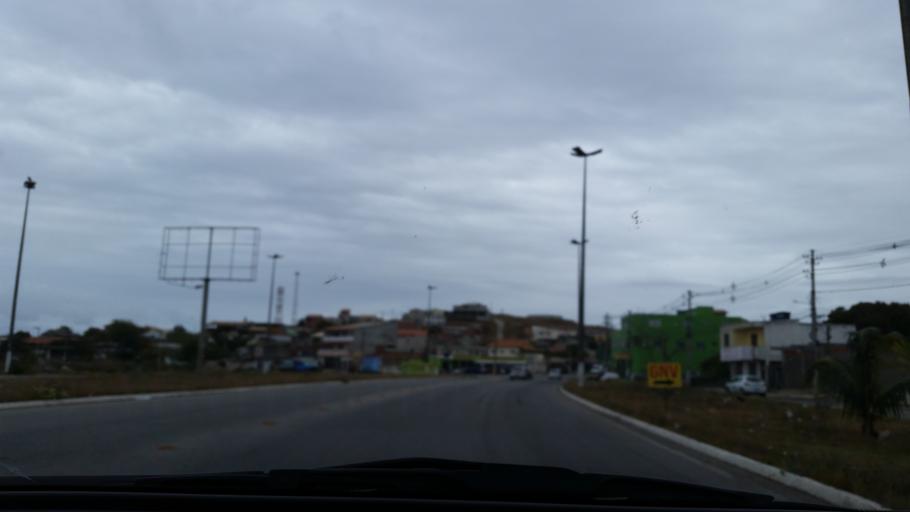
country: BR
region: Rio de Janeiro
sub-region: Cabo Frio
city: Cabo Frio
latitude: -22.8556
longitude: -42.0444
